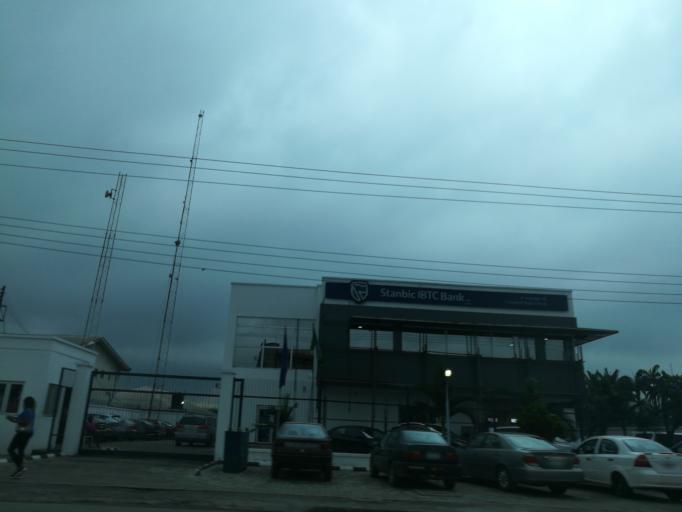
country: NG
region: Rivers
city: Port Harcourt
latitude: 4.8185
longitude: 7.0086
